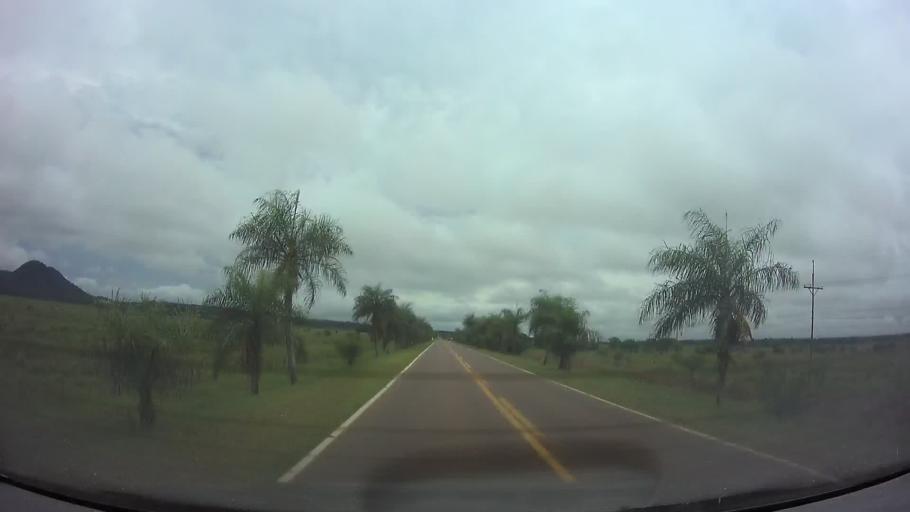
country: PY
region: Paraguari
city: Acahay
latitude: -25.8943
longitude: -57.1186
